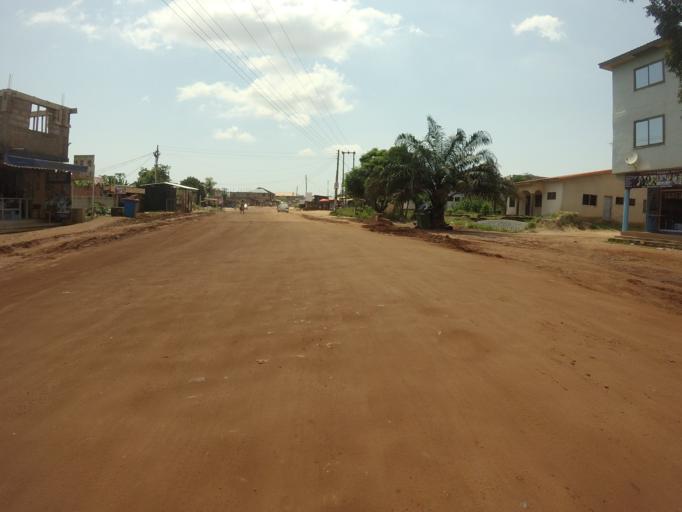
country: GH
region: Greater Accra
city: Gbawe
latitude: 5.6166
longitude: -0.3116
